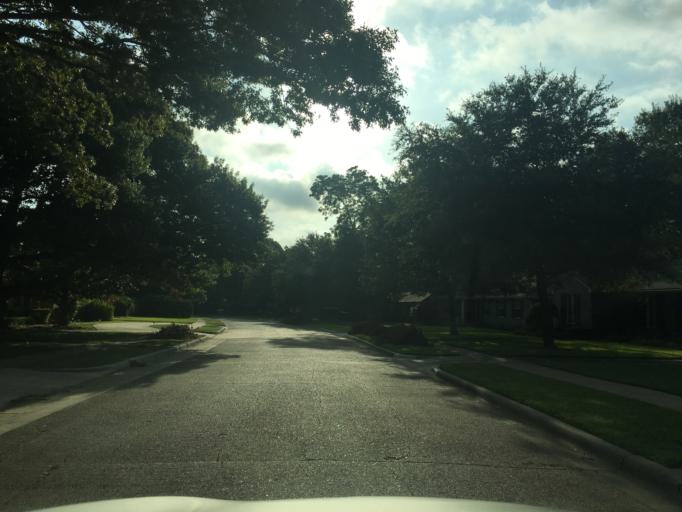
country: US
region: Texas
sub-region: Dallas County
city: Highland Park
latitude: 32.8501
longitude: -96.7507
